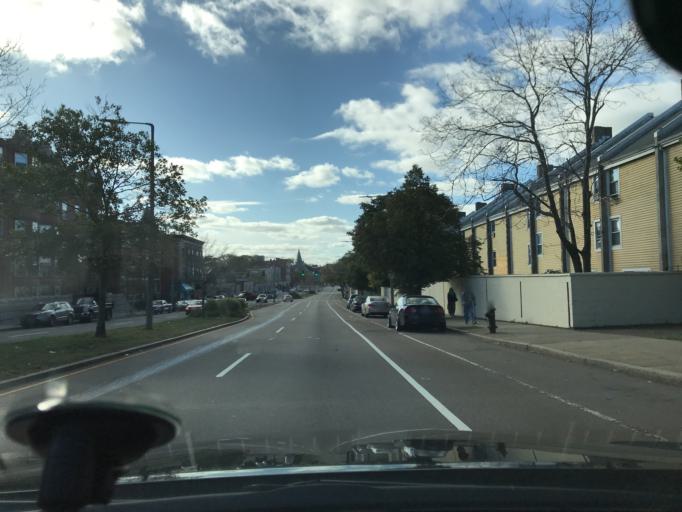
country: US
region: Massachusetts
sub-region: Suffolk County
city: South Boston
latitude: 42.3231
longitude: -71.0825
